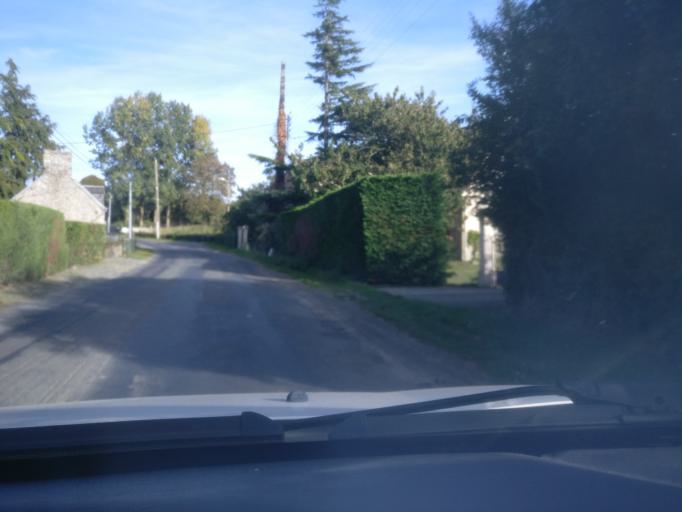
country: FR
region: Lower Normandy
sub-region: Departement de la Manche
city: Sartilly
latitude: 48.7080
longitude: -1.4769
